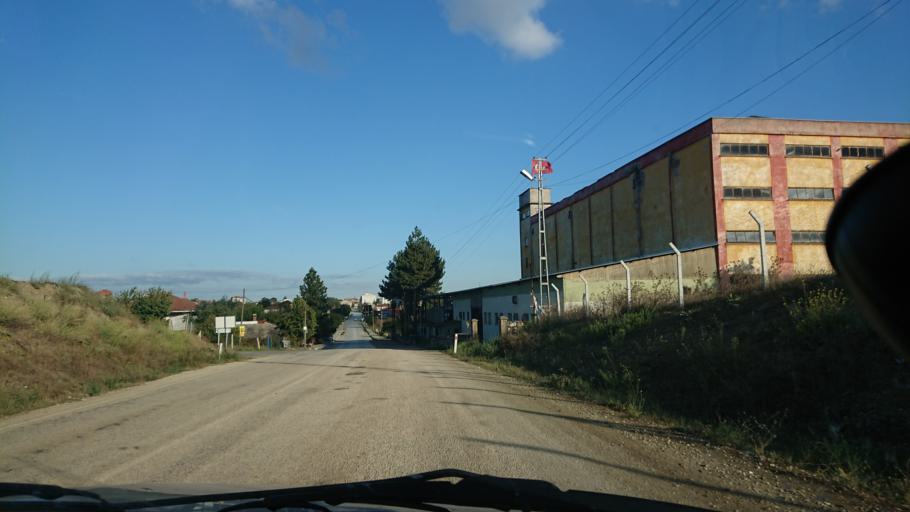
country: TR
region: Bilecik
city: Pazaryeri
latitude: 39.9996
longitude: 29.8880
